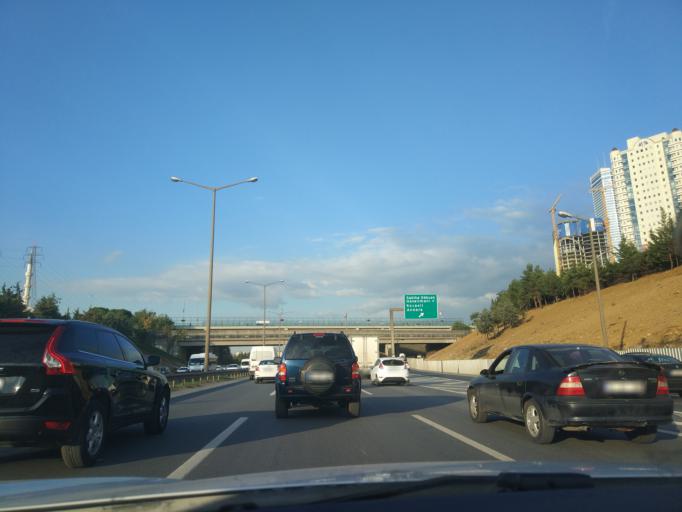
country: TR
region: Istanbul
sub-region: Atasehir
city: Atasehir
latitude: 40.9914
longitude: 29.1122
